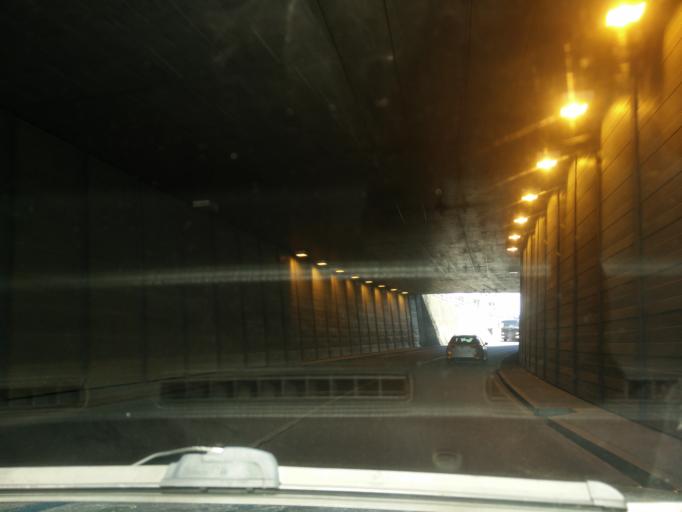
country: AT
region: Salzburg
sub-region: Politischer Bezirk Salzburg-Umgebung
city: Elsbethen
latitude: 47.7779
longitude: 13.0811
